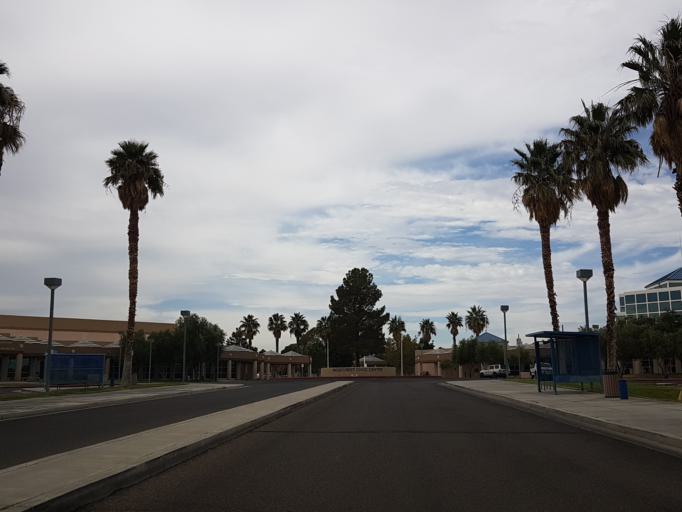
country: US
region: California
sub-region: Kern County
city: Ridgecrest
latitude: 35.6207
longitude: -117.6712
